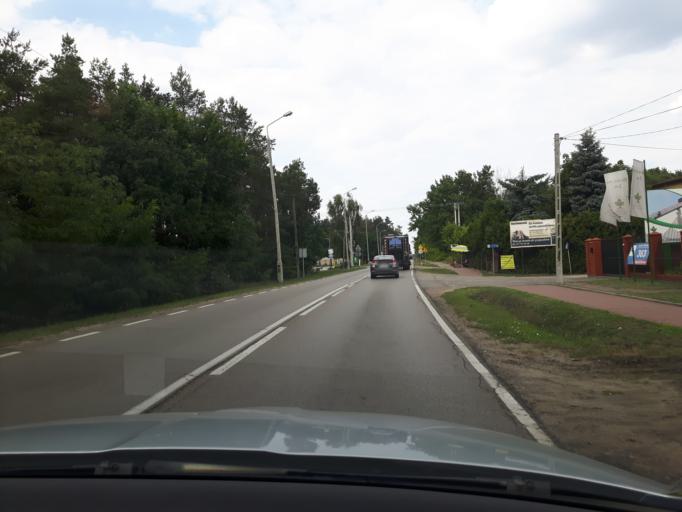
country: PL
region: Masovian Voivodeship
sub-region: Powiat legionowski
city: Stanislawow Pierwszy
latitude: 52.3833
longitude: 21.0292
